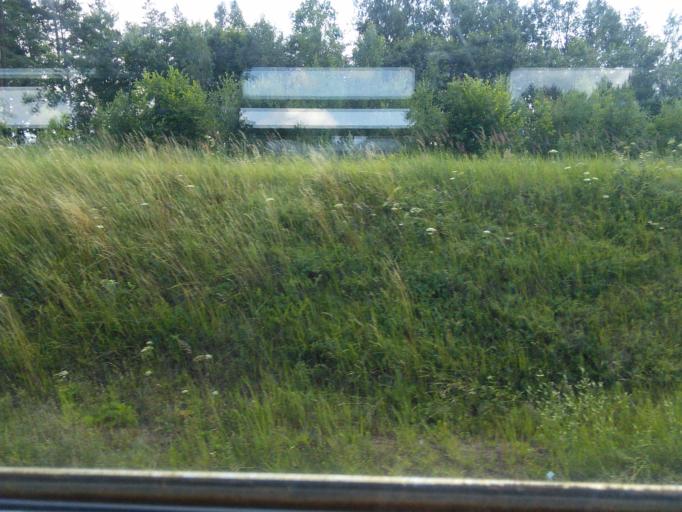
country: BY
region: Minsk
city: Maladzyechna
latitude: 54.2823
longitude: 26.9617
